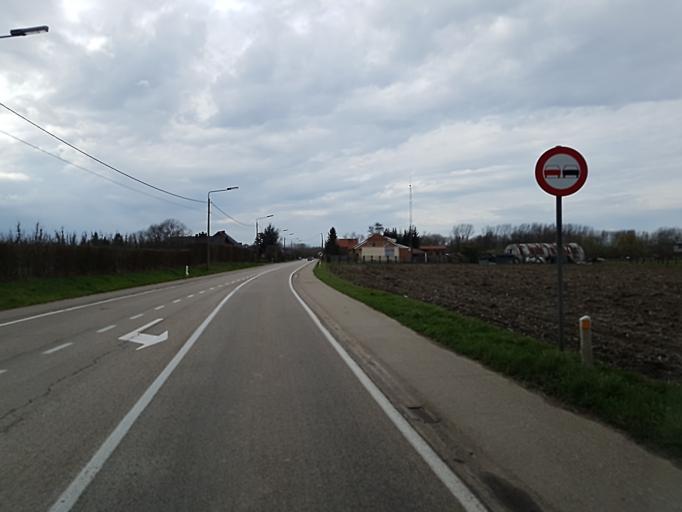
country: BE
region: Flanders
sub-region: Provincie Limburg
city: Herk-de-Stad
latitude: 50.9223
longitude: 5.2233
